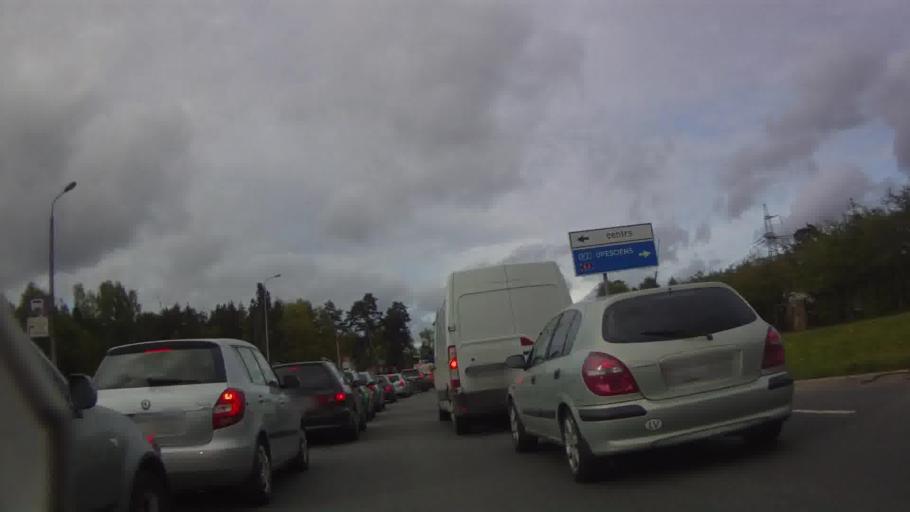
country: LV
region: Stopini
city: Ulbroka
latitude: 56.9588
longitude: 24.2287
